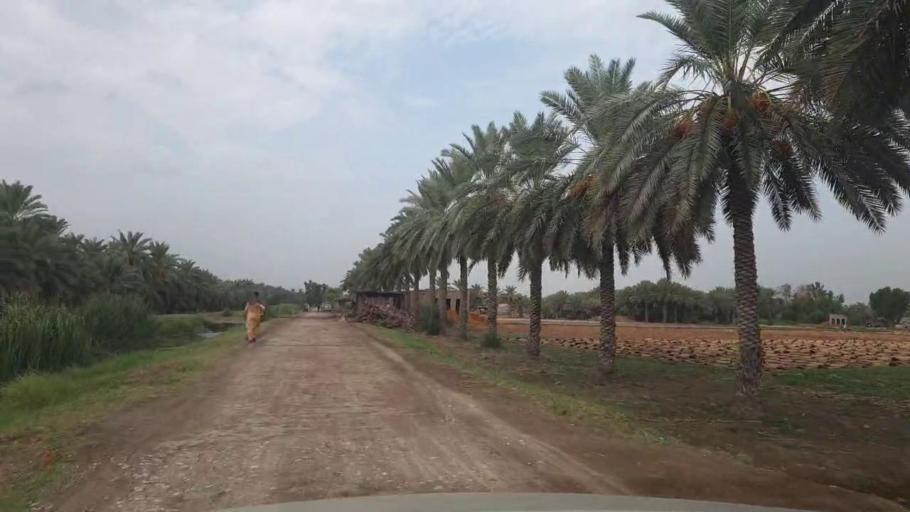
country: PK
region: Sindh
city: Khairpur
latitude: 27.6031
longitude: 68.8308
